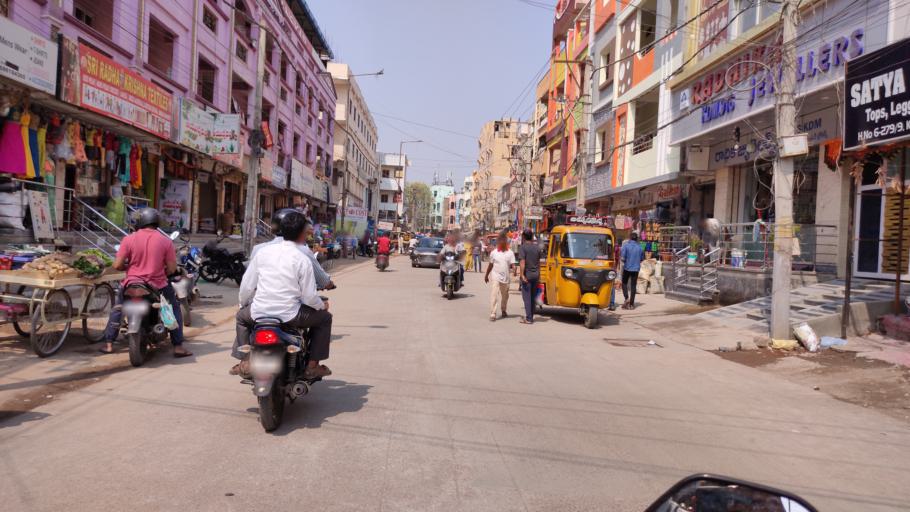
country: IN
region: Telangana
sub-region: Rangareddi
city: Quthbullapur
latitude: 17.4957
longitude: 78.4561
